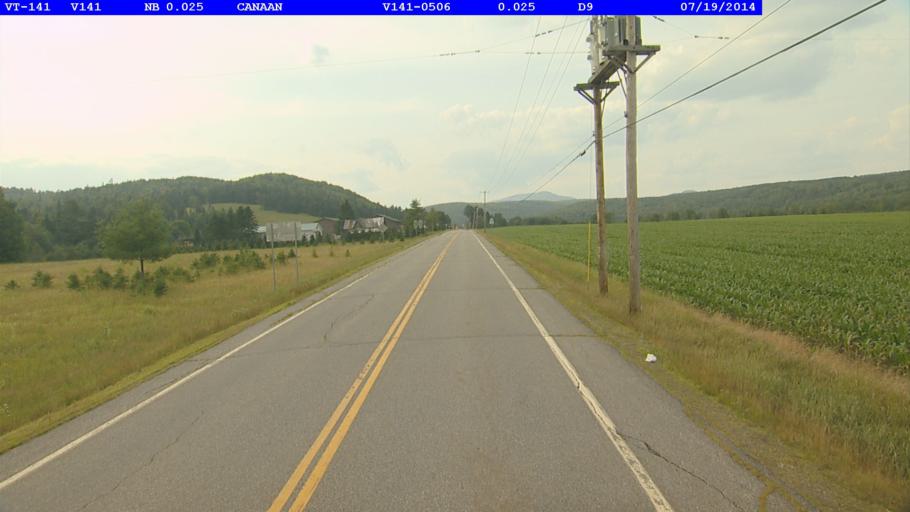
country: US
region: New Hampshire
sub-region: Coos County
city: Colebrook
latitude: 45.0073
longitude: -71.5560
